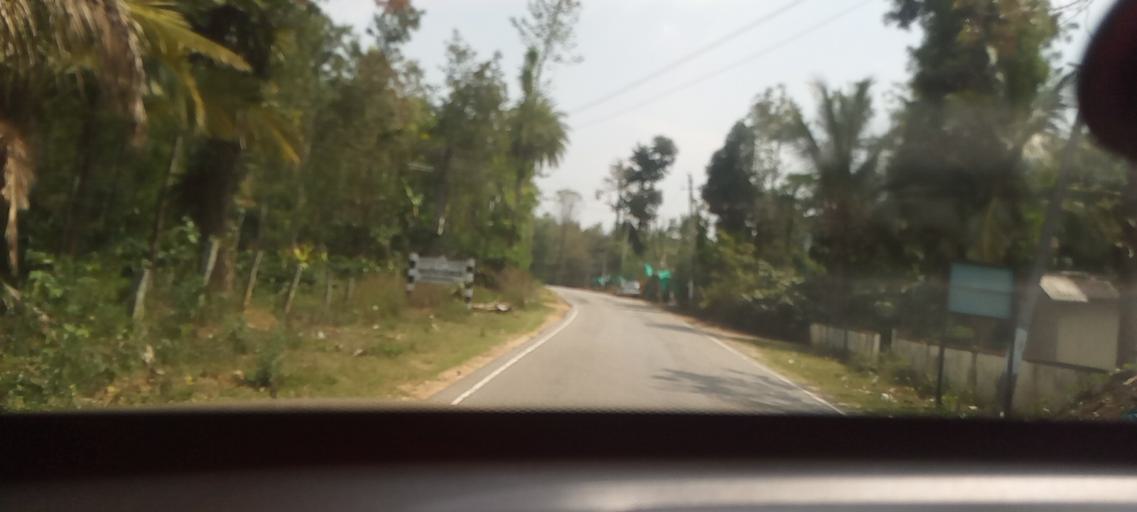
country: IN
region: Karnataka
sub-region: Chikmagalur
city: Mudigere
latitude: 13.2839
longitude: 75.6021
